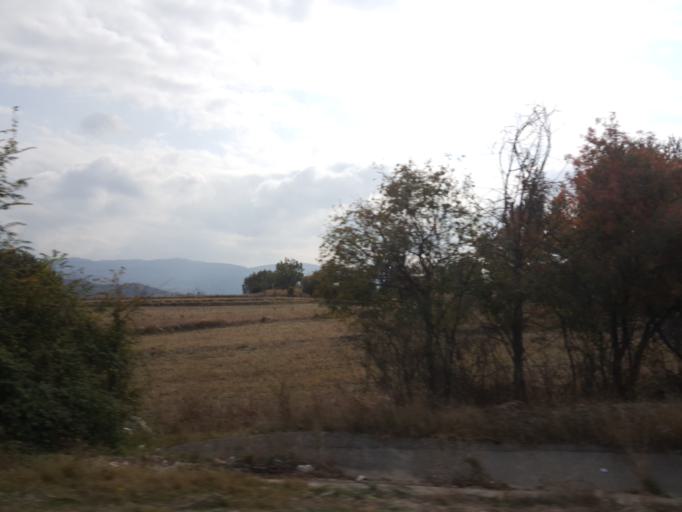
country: TR
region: Sinop
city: Sarayduzu
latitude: 41.3427
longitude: 34.8081
